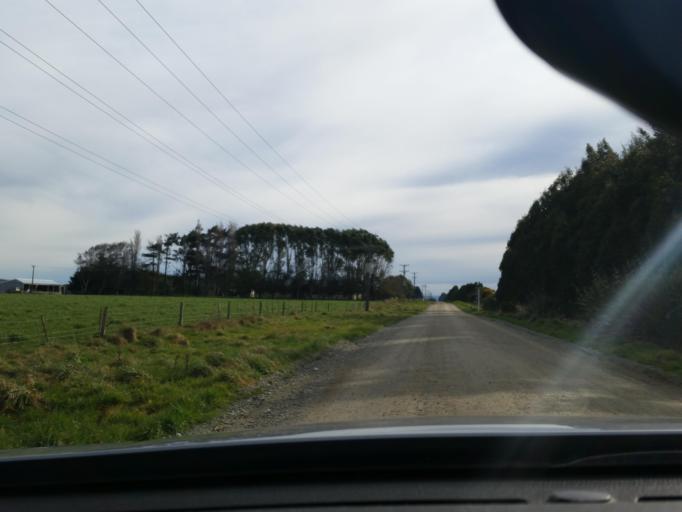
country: NZ
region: Southland
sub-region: Invercargill City
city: Invercargill
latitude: -46.3382
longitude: 168.4535
